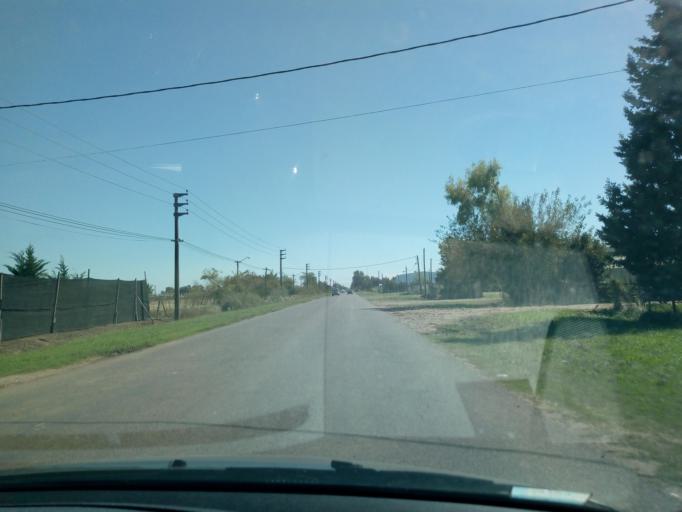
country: AR
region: Buenos Aires
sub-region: Partido de La Plata
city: La Plata
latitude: -35.0075
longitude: -58.0318
